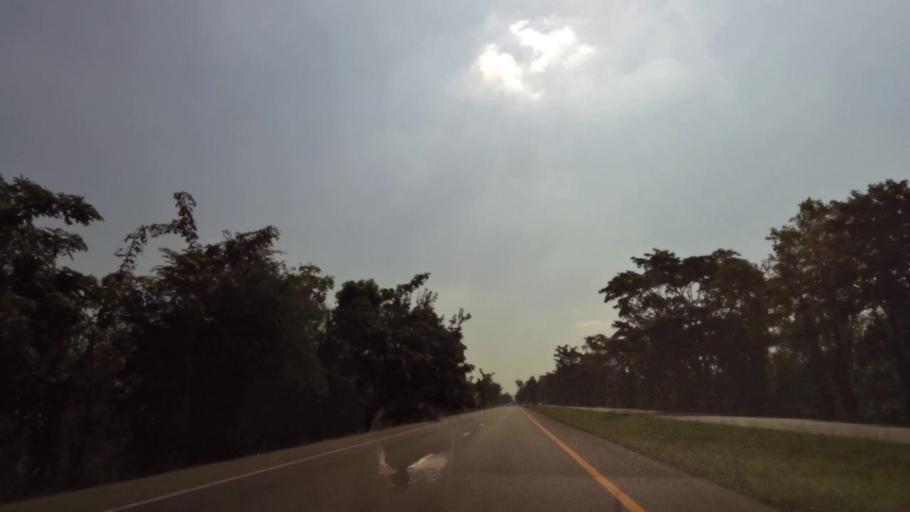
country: TH
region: Phichit
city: Bueng Na Rang
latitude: 16.2095
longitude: 100.1273
